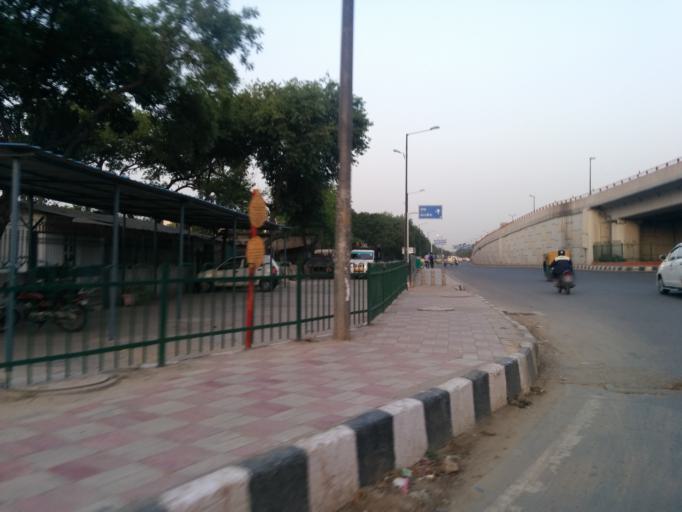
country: IN
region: NCT
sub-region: New Delhi
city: New Delhi
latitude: 28.5701
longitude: 77.1995
